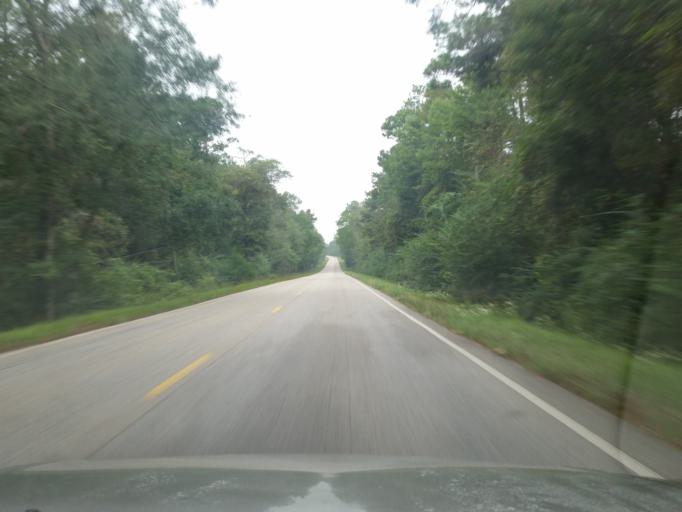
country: US
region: Florida
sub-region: Escambia County
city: Cantonment
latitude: 30.6047
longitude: -87.4051
